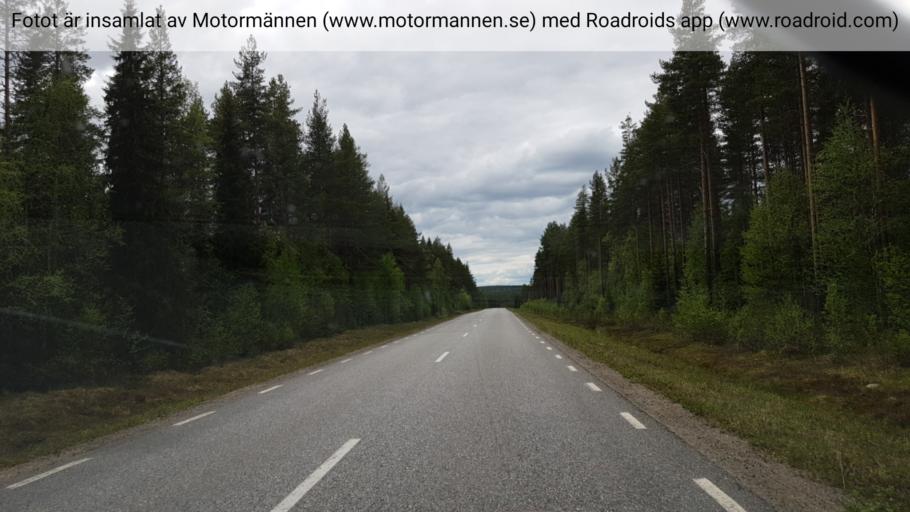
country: SE
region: Vaesterbotten
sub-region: Skelleftea Kommun
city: Langsele
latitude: 64.6110
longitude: 19.9555
